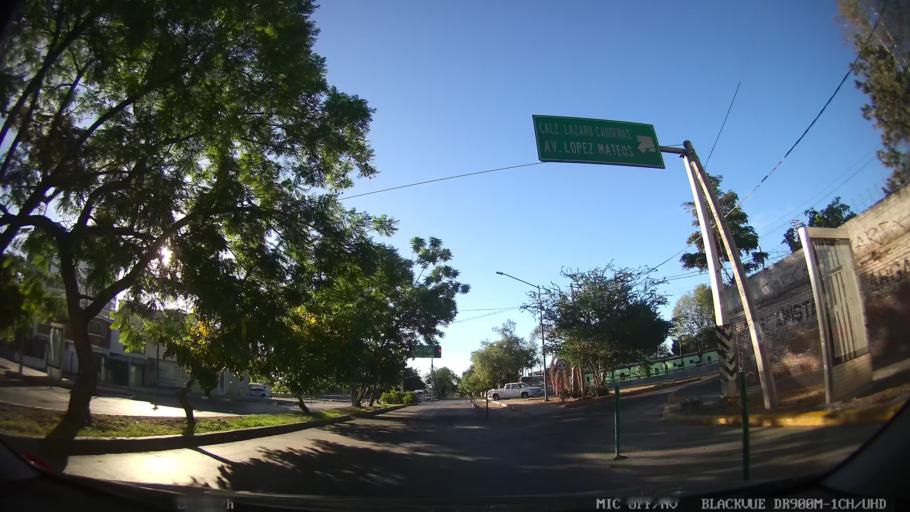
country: MX
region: Jalisco
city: Guadalajara
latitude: 20.6657
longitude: -103.3739
